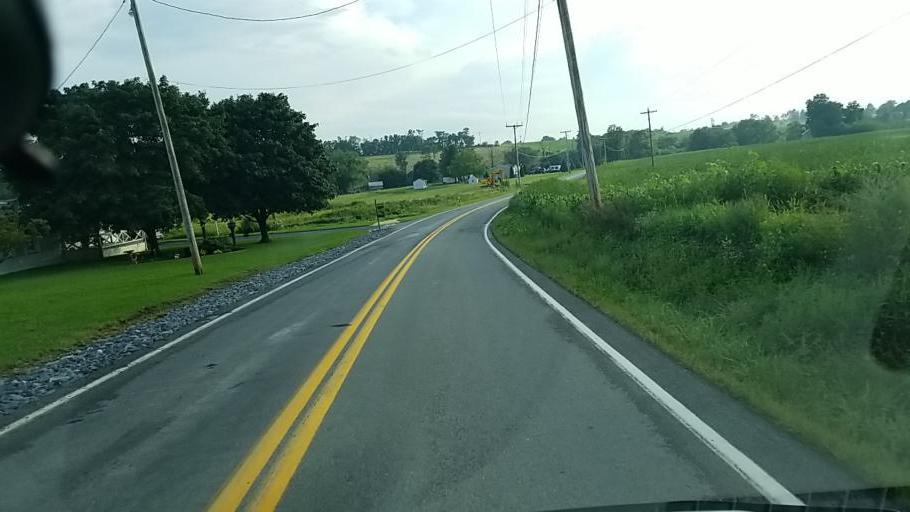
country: US
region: Pennsylvania
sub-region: Cumberland County
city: Newville
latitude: 40.2179
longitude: -77.4644
